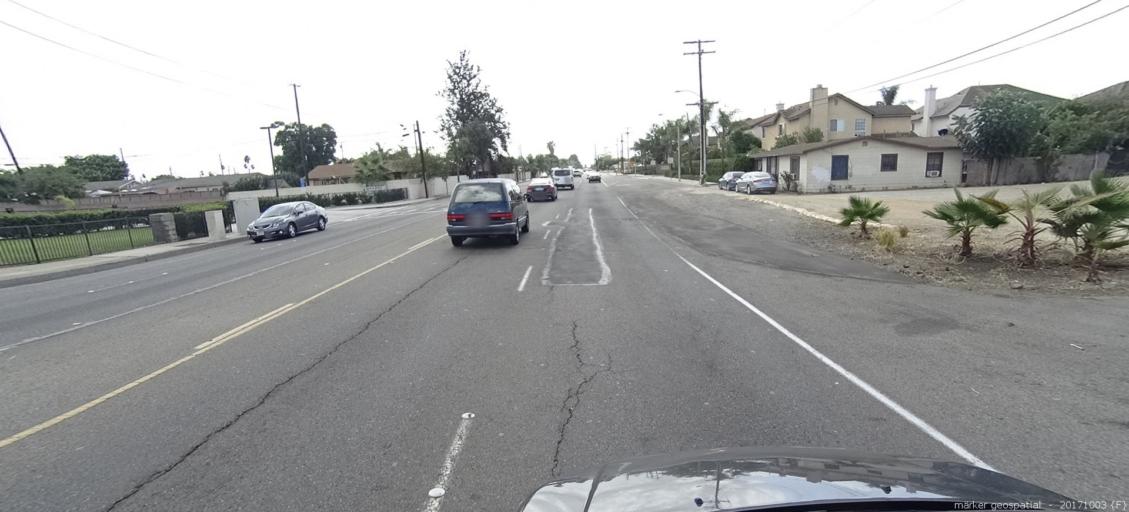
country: US
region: California
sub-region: Orange County
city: Garden Grove
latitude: 33.7732
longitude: -117.9031
